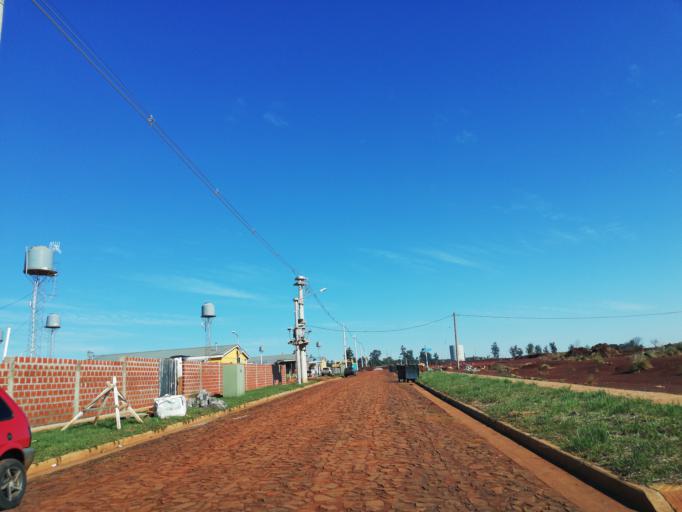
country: AR
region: Misiones
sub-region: Departamento de Capital
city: Posadas
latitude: -27.4145
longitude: -55.9917
